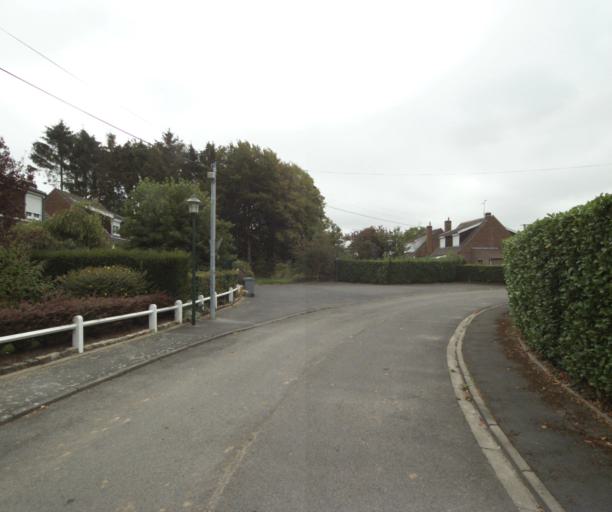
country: FR
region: Nord-Pas-de-Calais
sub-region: Departement du Nord
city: Chereng
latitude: 50.6163
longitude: 3.2113
